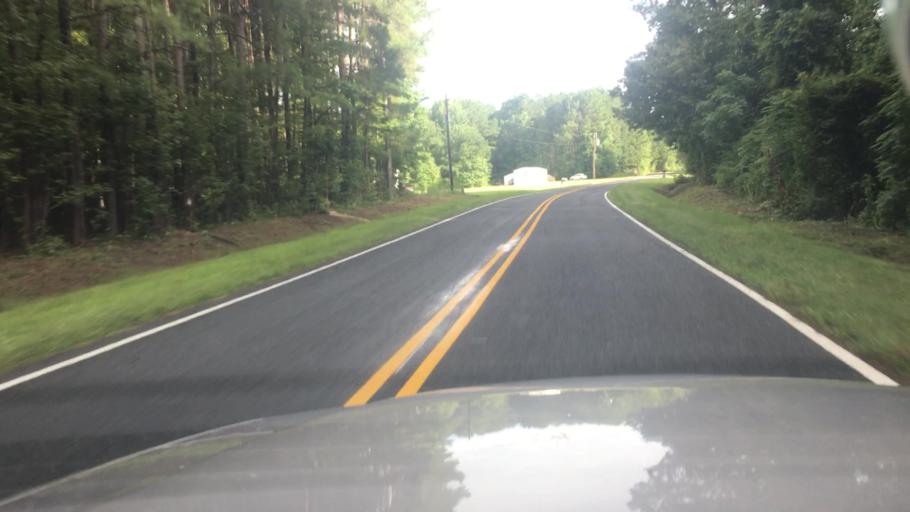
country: US
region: North Carolina
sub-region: Cumberland County
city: Eastover
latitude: 35.1593
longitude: -78.8537
